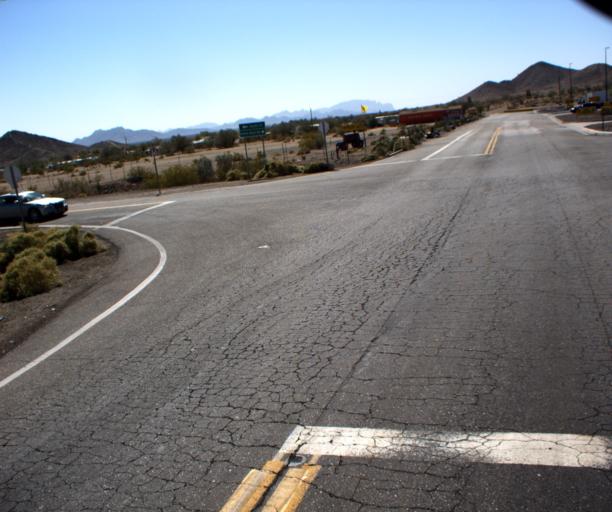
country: US
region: Arizona
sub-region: La Paz County
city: Quartzsite
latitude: 33.6582
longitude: -114.2406
